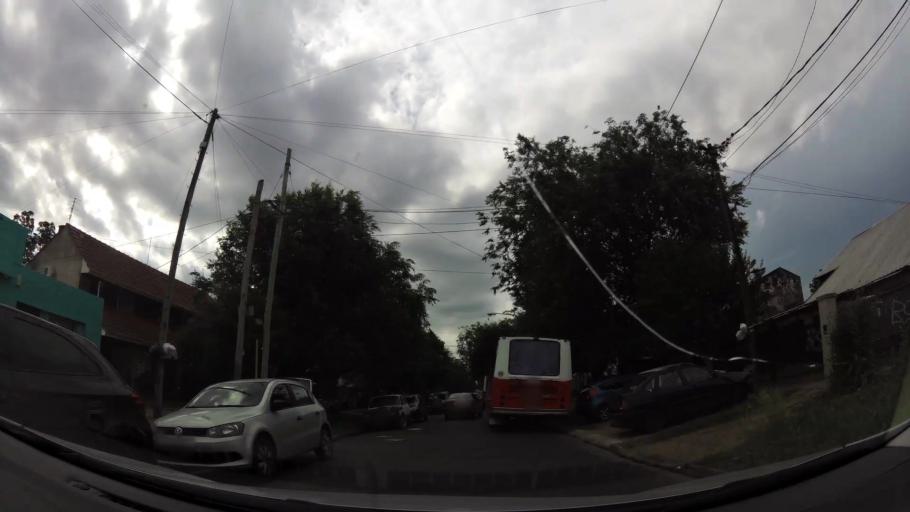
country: AR
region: Buenos Aires
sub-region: Partido de Tigre
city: Tigre
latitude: -34.4709
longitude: -58.6469
